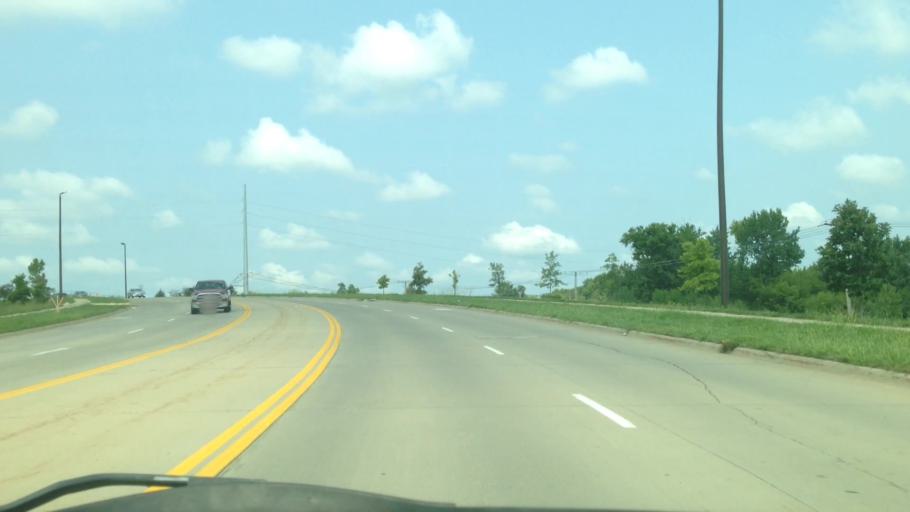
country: US
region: Iowa
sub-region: Linn County
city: Cedar Rapids
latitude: 41.9449
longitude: -91.6915
